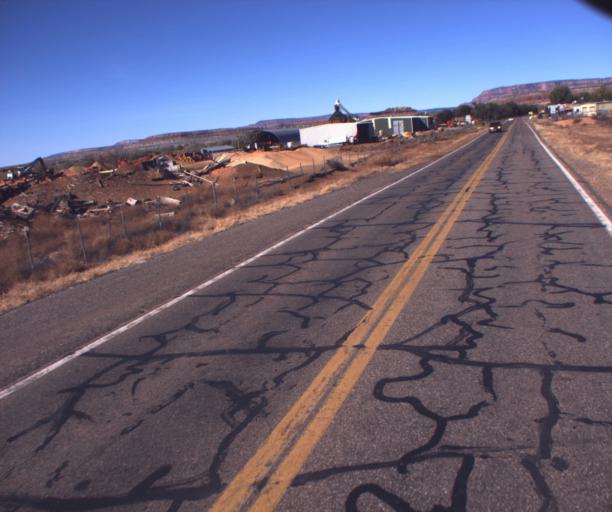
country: US
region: Arizona
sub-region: Coconino County
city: Fredonia
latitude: 36.9386
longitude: -112.5181
